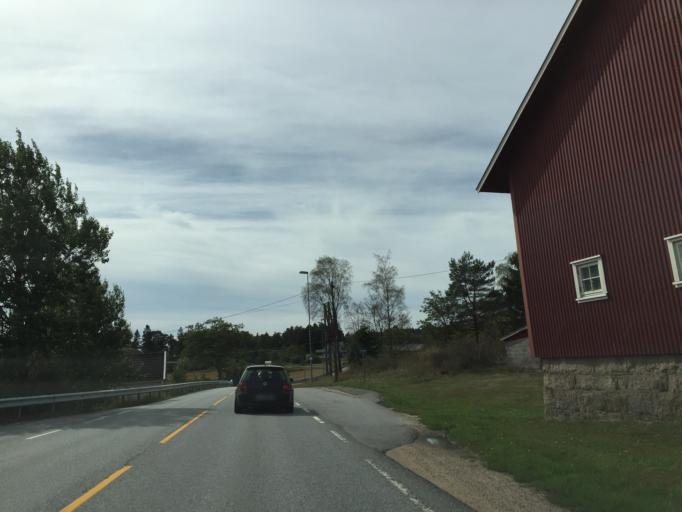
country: NO
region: Ostfold
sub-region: Fredrikstad
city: Fredrikstad
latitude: 59.2775
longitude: 10.9015
